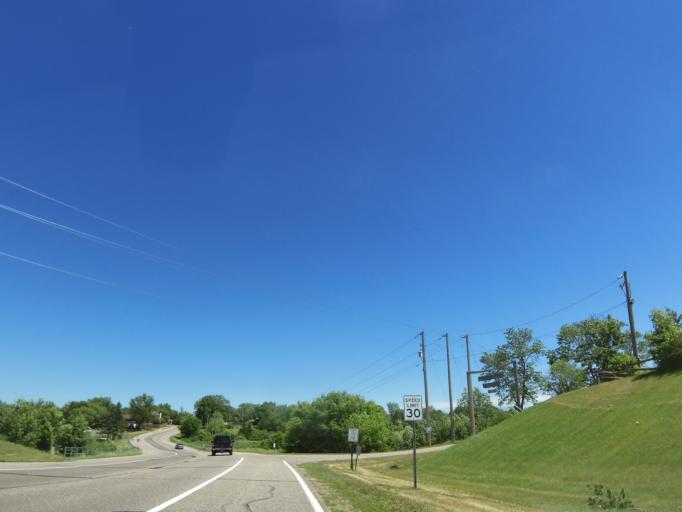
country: US
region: Minnesota
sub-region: Becker County
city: Frazee
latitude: 46.7228
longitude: -95.7108
